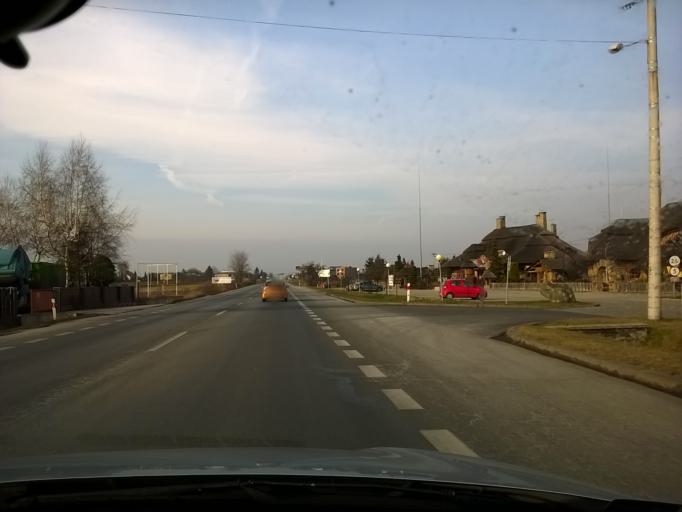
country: PL
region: Silesian Voivodeship
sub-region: Powiat gliwicki
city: Paniowki
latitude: 50.2299
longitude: 18.7989
